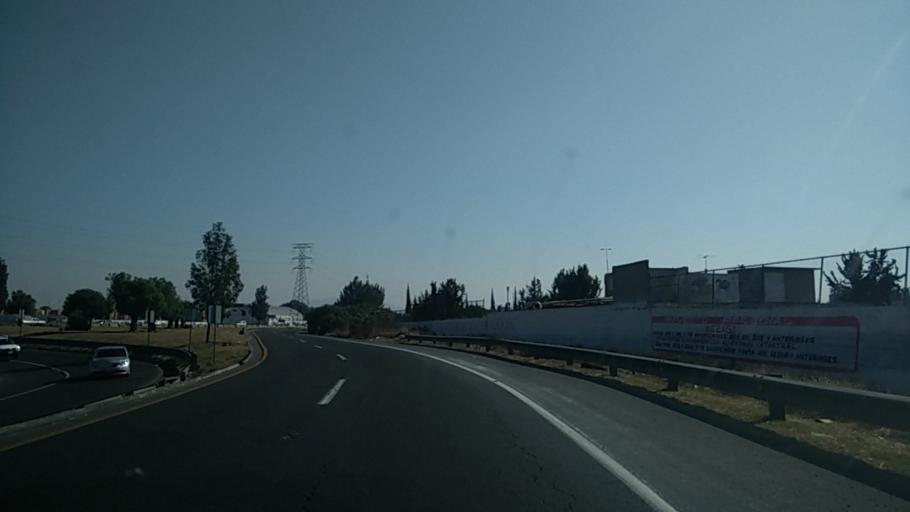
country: MX
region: Mexico
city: Santo Tomas Chiconautla
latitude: 19.6137
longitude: -99.0304
